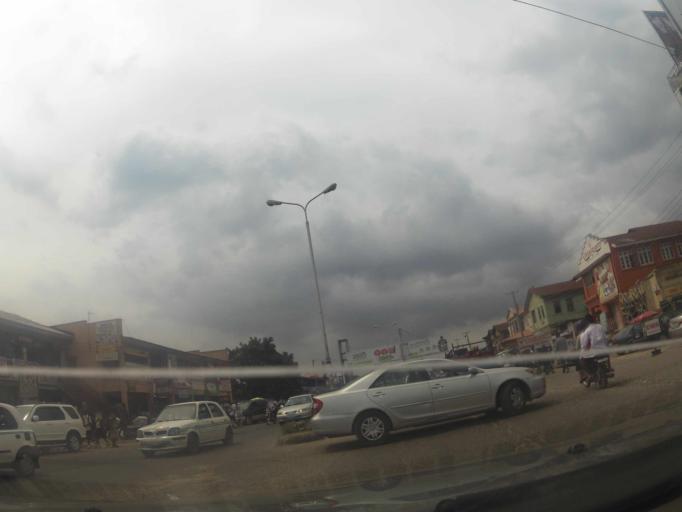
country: NG
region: Oyo
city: Ibadan
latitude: 7.4038
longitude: 3.8901
